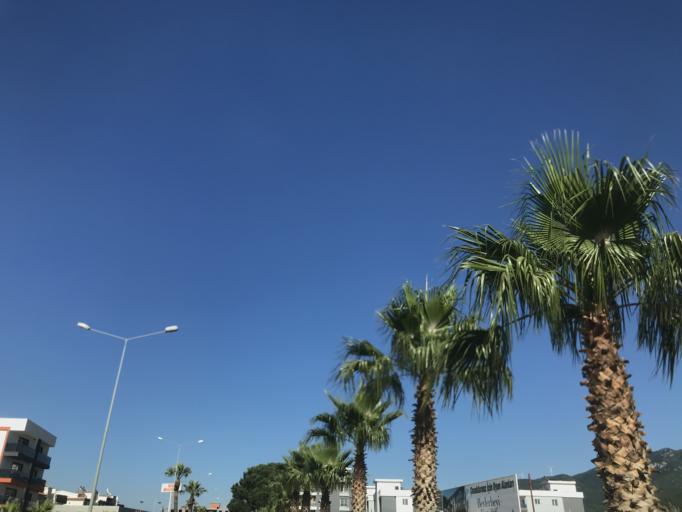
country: TR
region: Aydin
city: Davutlar
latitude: 37.7333
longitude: 27.2806
